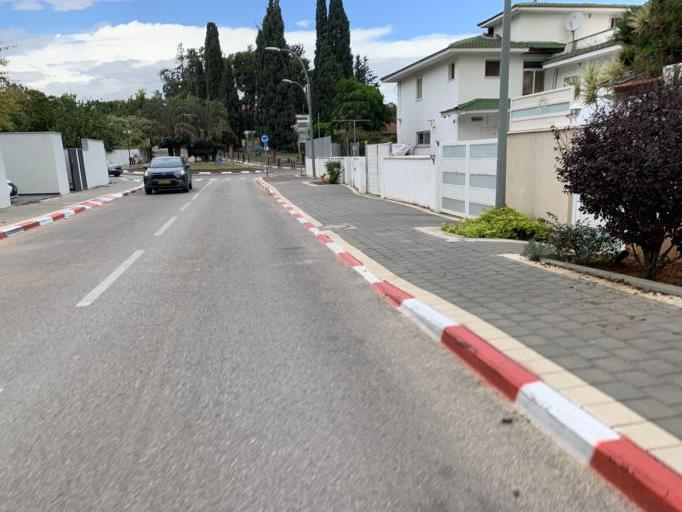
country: IL
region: Central District
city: Hod HaSharon
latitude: 32.1556
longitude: 34.8869
